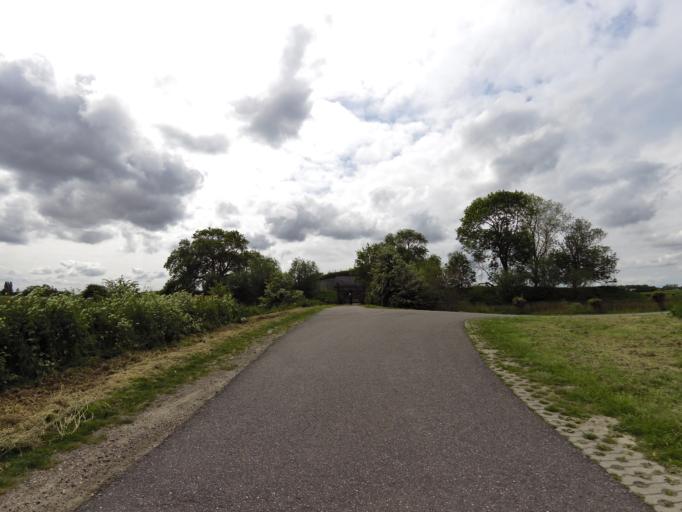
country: NL
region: South Holland
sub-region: Gemeente Brielle
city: Brielle
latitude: 51.8823
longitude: 4.1578
